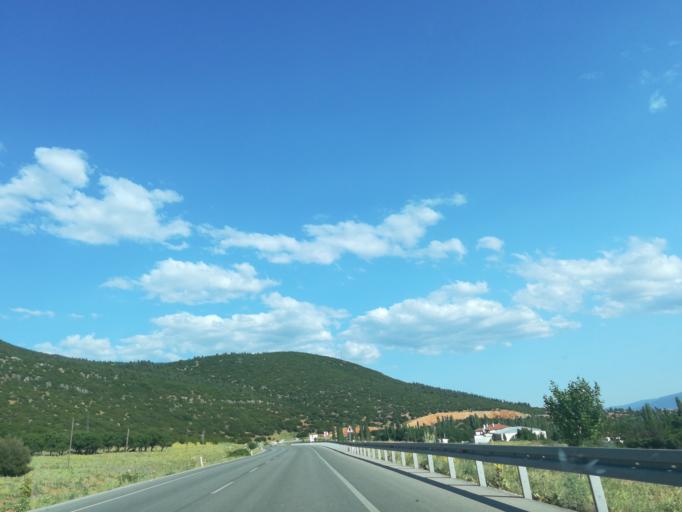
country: TR
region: Denizli
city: Ishakli
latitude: 38.1630
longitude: 30.0777
